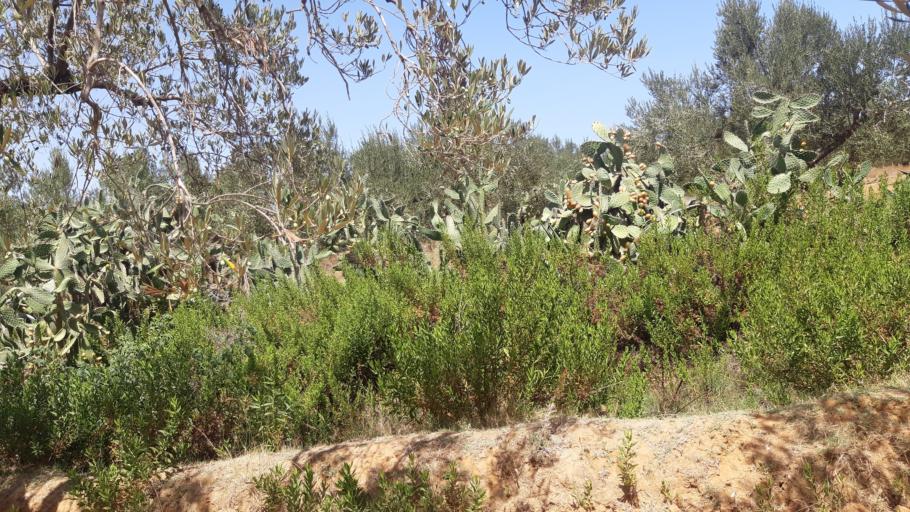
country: TN
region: Al Munastir
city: Qusaybat al Madyuni
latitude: 35.6771
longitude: 10.8573
